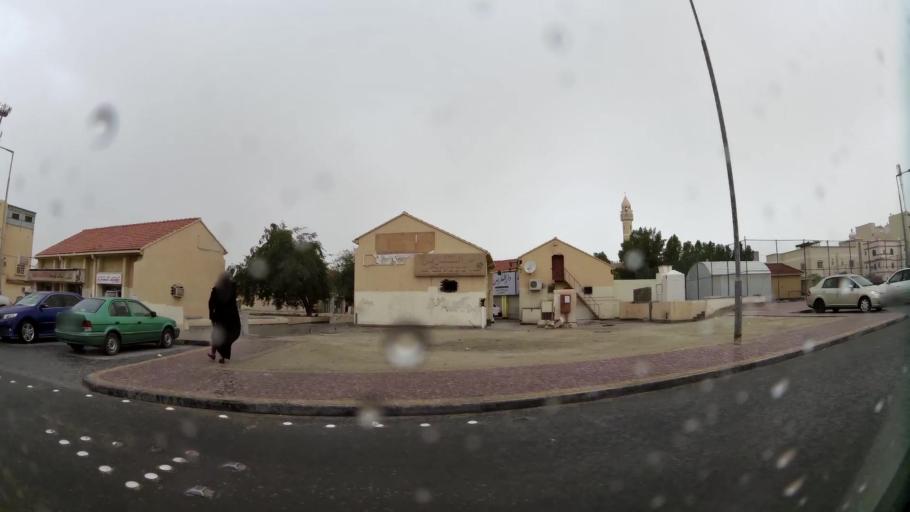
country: BH
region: Northern
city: Madinat `Isa
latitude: 26.1570
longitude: 50.5694
